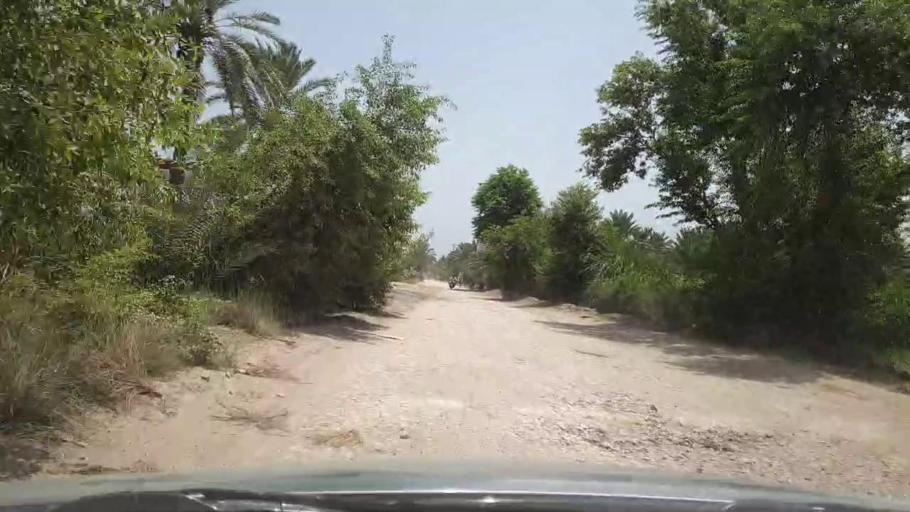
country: PK
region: Sindh
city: Pano Aqil
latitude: 27.8592
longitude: 69.0917
